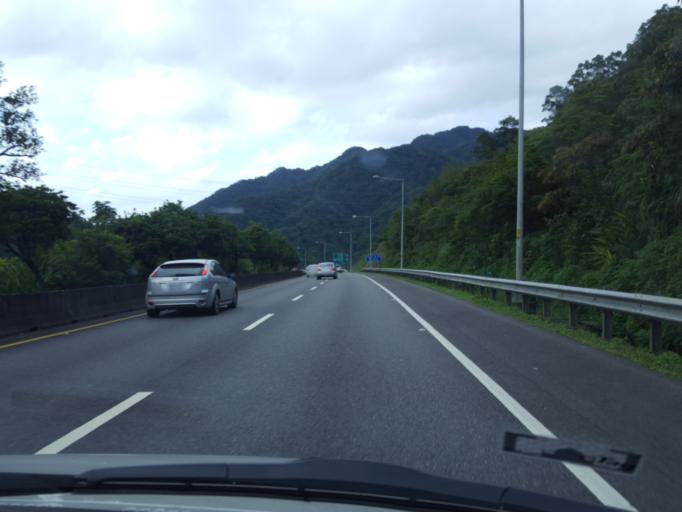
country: TW
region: Taipei
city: Taipei
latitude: 24.9761
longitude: 121.6774
